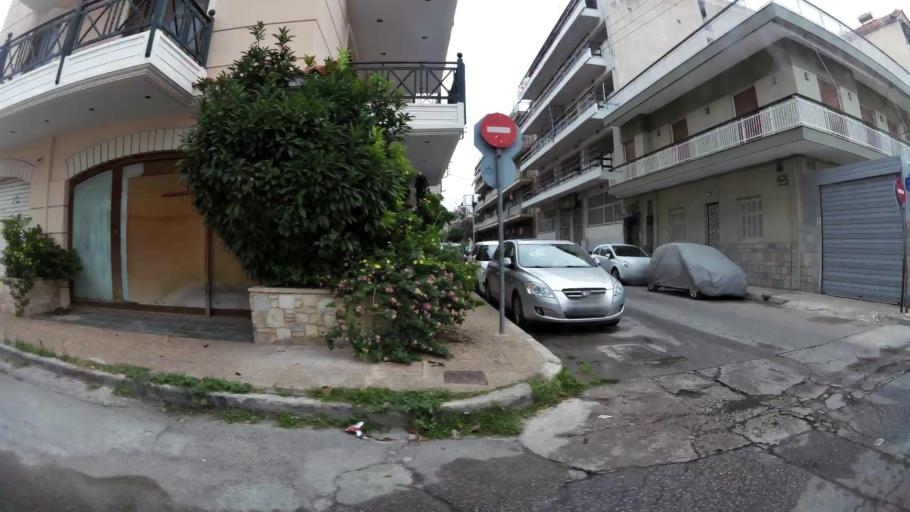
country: GR
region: Attica
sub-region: Nomarchia Athinas
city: Ilion
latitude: 38.0318
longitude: 23.7037
